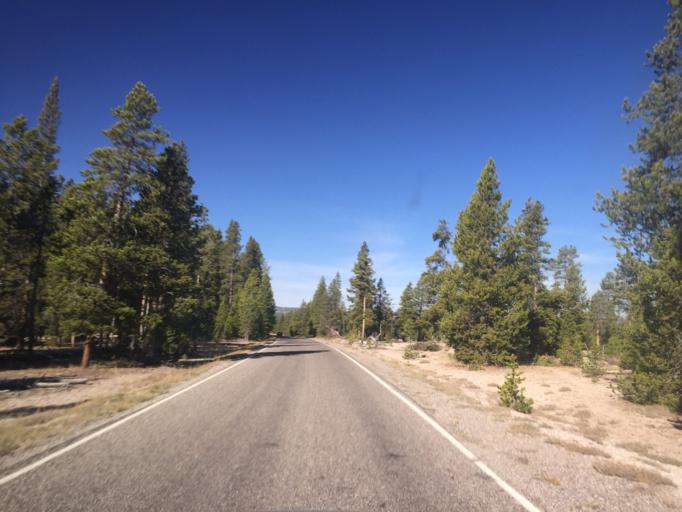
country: US
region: Montana
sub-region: Gallatin County
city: West Yellowstone
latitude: 44.5469
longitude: -110.7958
